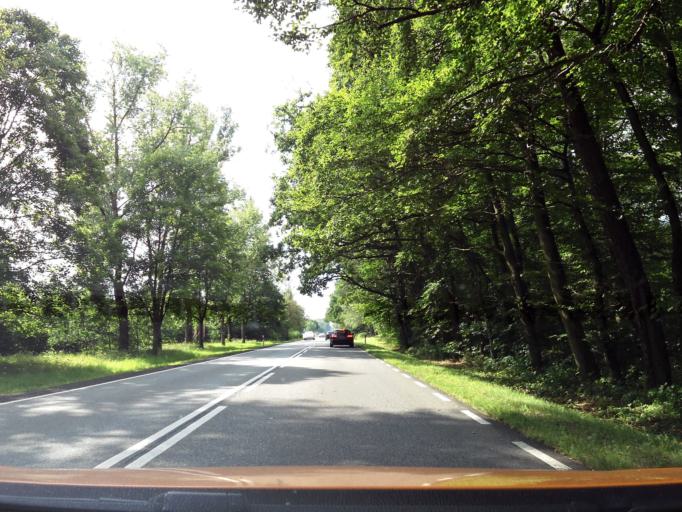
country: PL
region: West Pomeranian Voivodeship
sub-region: Powiat gryficki
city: Ploty
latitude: 53.8209
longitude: 15.2829
